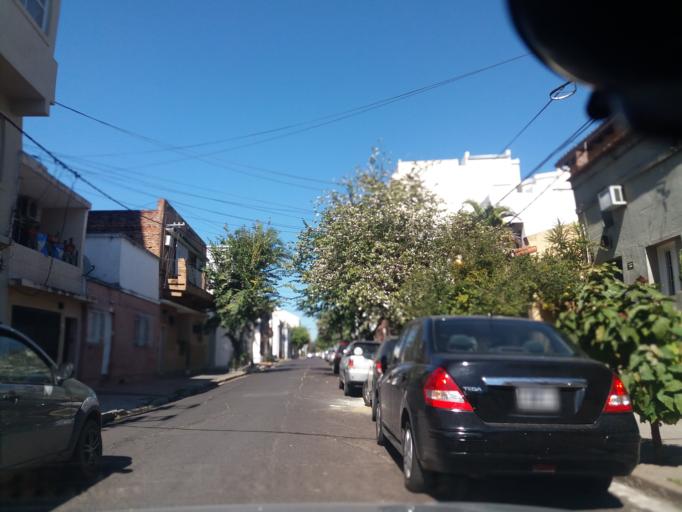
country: AR
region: Corrientes
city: Corrientes
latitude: -27.4682
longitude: -58.8443
